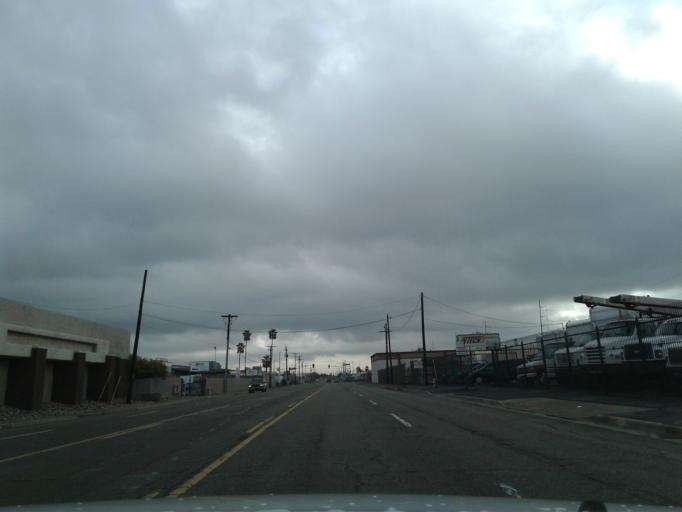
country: US
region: Arizona
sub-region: Maricopa County
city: Phoenix
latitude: 33.4413
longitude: -112.1027
